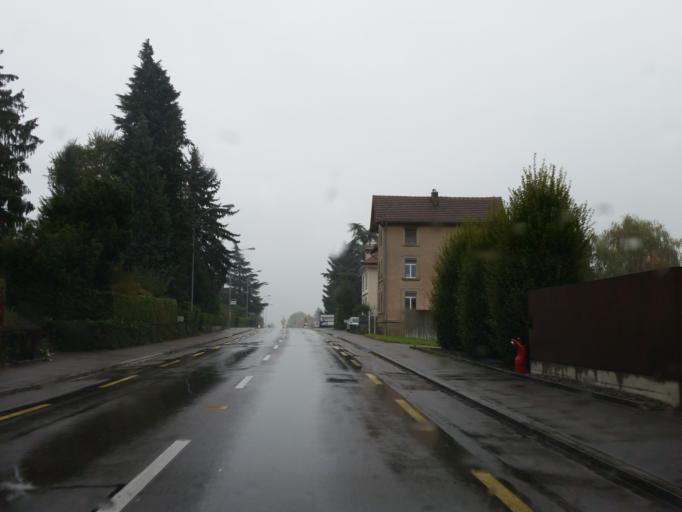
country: CH
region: Thurgau
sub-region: Arbon District
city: Egnach
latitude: 47.5272
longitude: 9.3756
